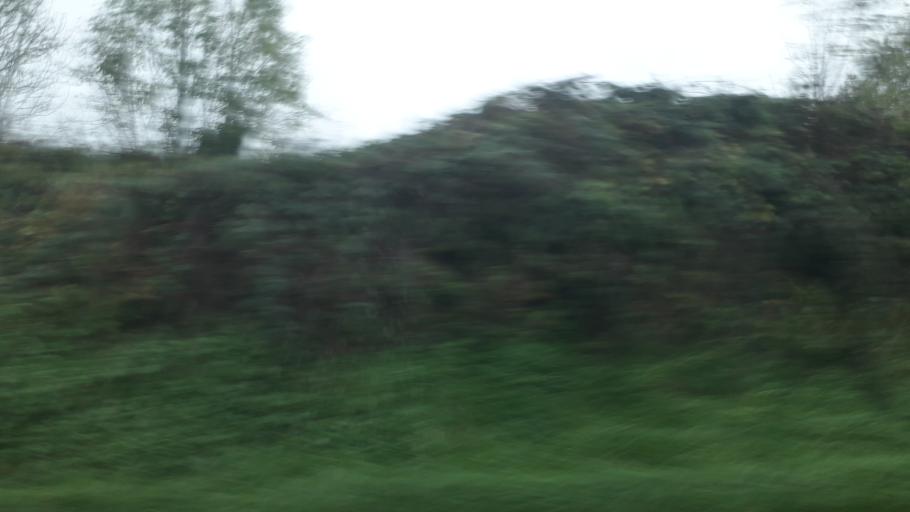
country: IE
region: Leinster
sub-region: An Longfort
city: Edgeworthstown
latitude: 53.6877
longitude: -7.5955
